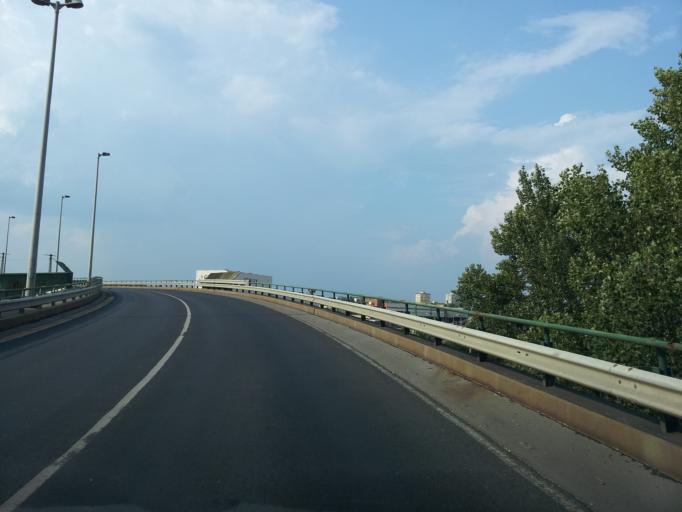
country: HU
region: Budapest
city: Budapest XXII. keruelet
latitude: 47.4066
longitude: 19.0252
